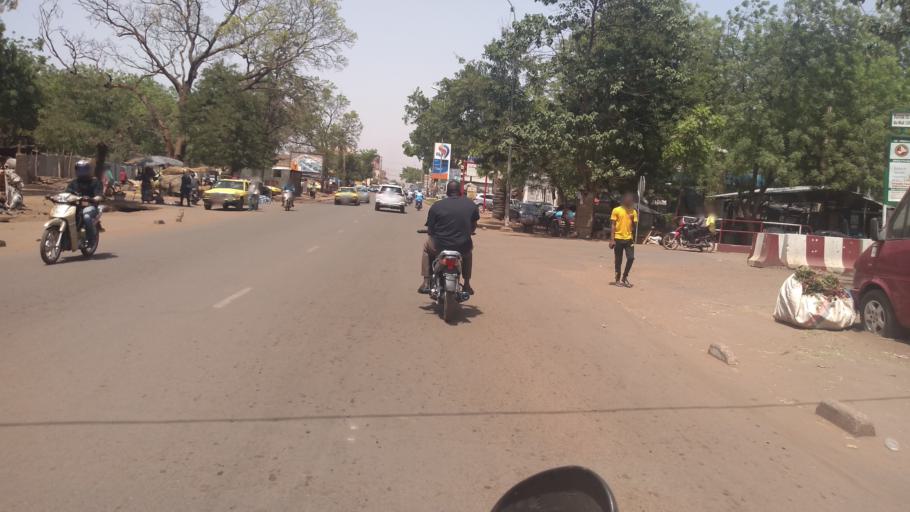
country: ML
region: Bamako
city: Bamako
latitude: 12.6432
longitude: -8.0174
